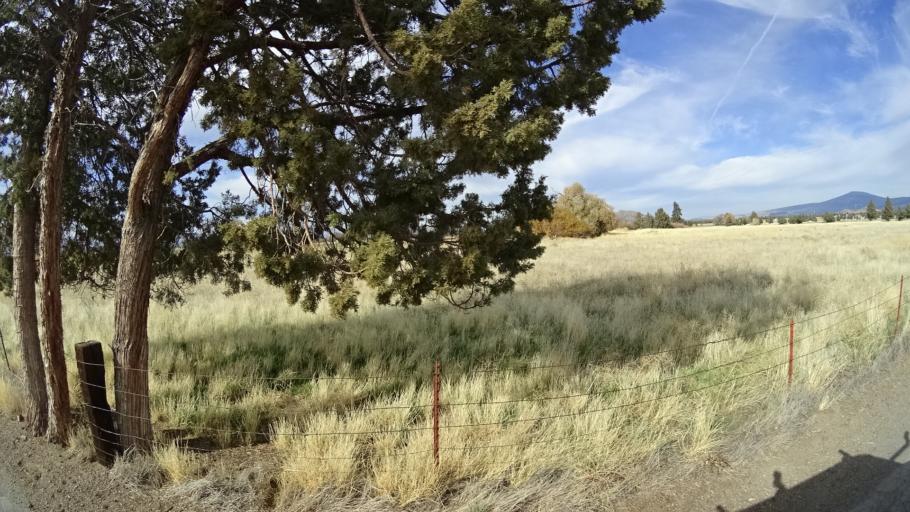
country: US
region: California
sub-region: Siskiyou County
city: Montague
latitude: 41.6175
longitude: -122.3818
